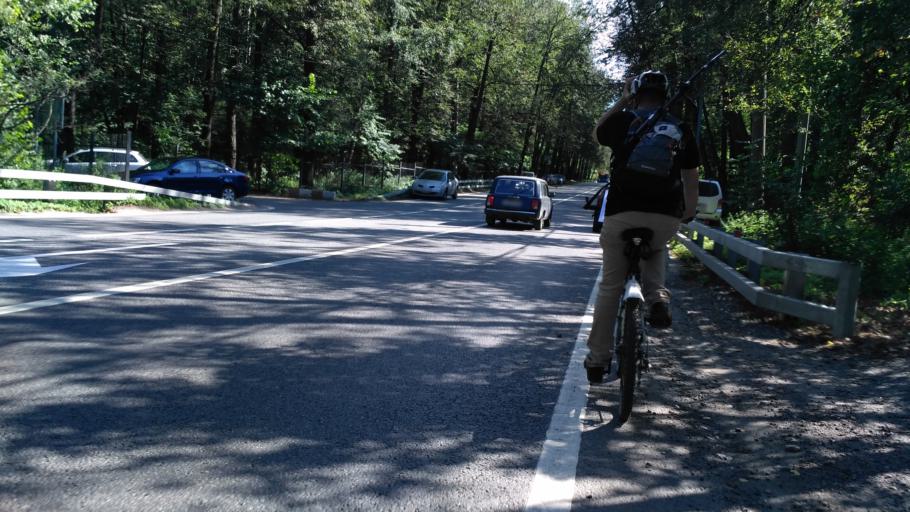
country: RU
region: Moskovskaya
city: Izmaylovo
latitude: 55.7767
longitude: 37.7653
